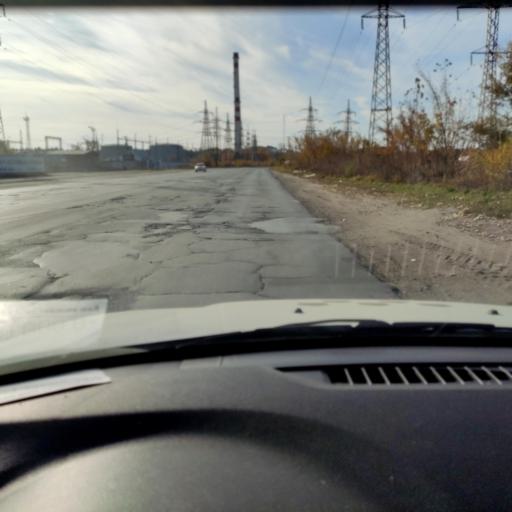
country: RU
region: Samara
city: Tol'yatti
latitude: 53.5181
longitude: 49.4664
